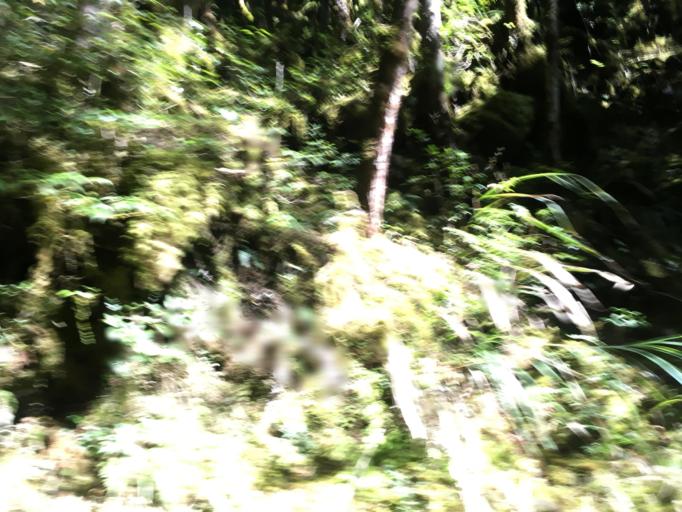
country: TW
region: Taiwan
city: Daxi
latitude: 24.5916
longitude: 121.4170
